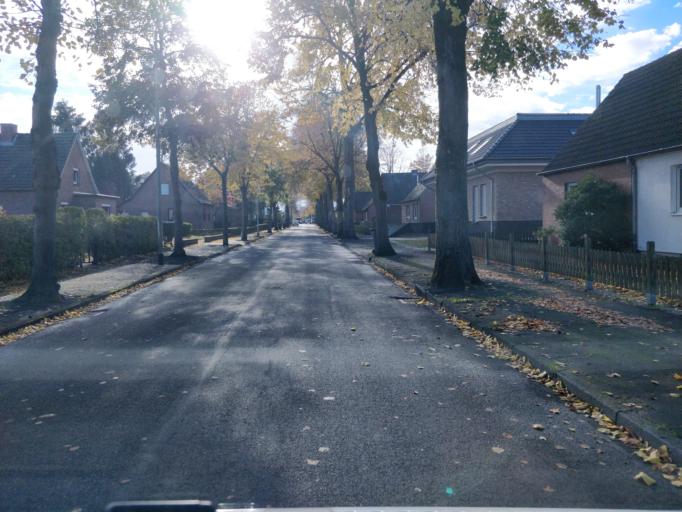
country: DE
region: North Rhine-Westphalia
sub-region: Regierungsbezirk Dusseldorf
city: Emmerich
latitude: 51.8473
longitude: 6.2453
